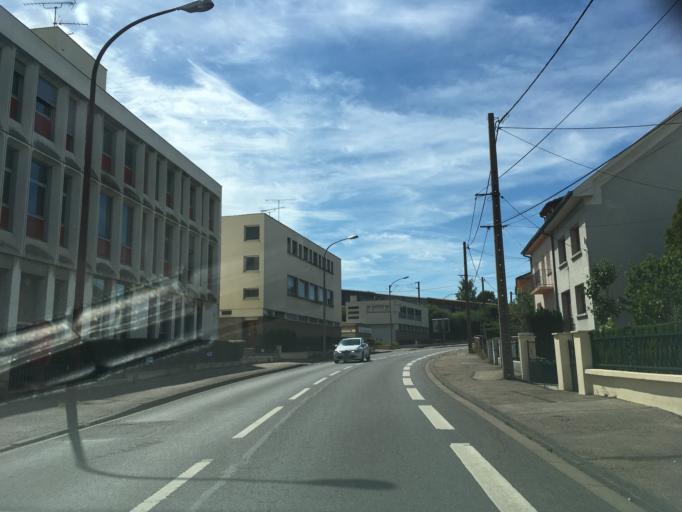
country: FR
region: Lorraine
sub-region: Departement de la Moselle
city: Montigny-les-Metz
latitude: 49.0904
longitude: 6.1808
